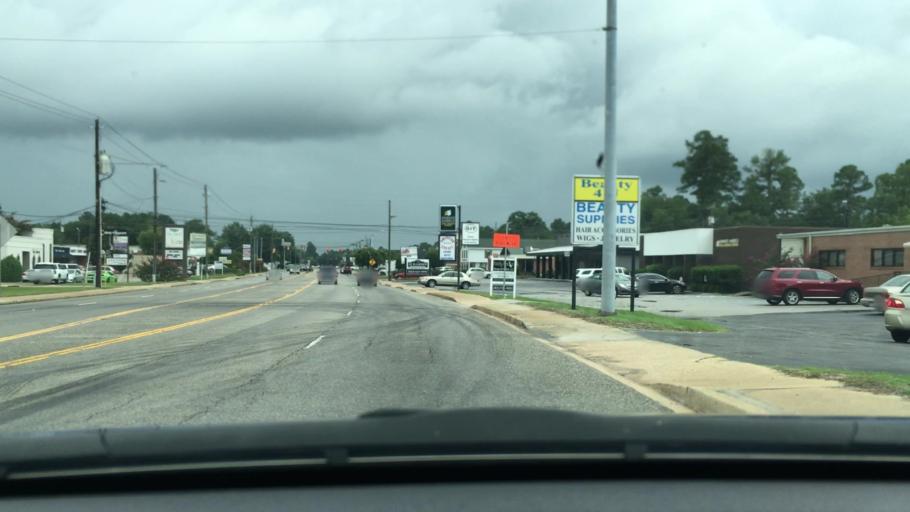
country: US
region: South Carolina
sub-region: Sumter County
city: Sumter
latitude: 33.9441
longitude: -80.3727
